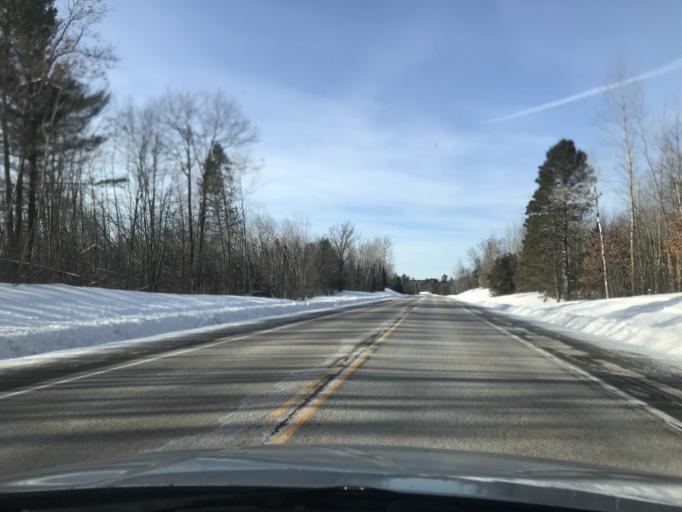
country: US
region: Wisconsin
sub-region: Oconto County
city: Gillett
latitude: 45.1234
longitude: -88.3959
